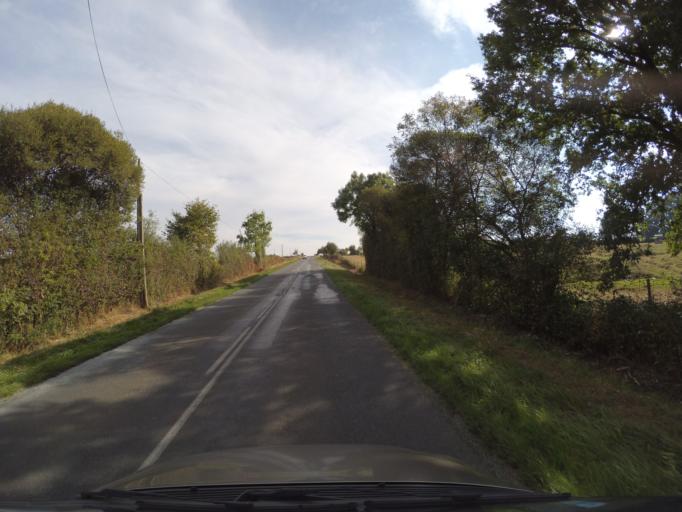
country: FR
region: Pays de la Loire
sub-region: Departement de Maine-et-Loire
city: La Chapelle-du-Genet
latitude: 47.1845
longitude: -1.0556
